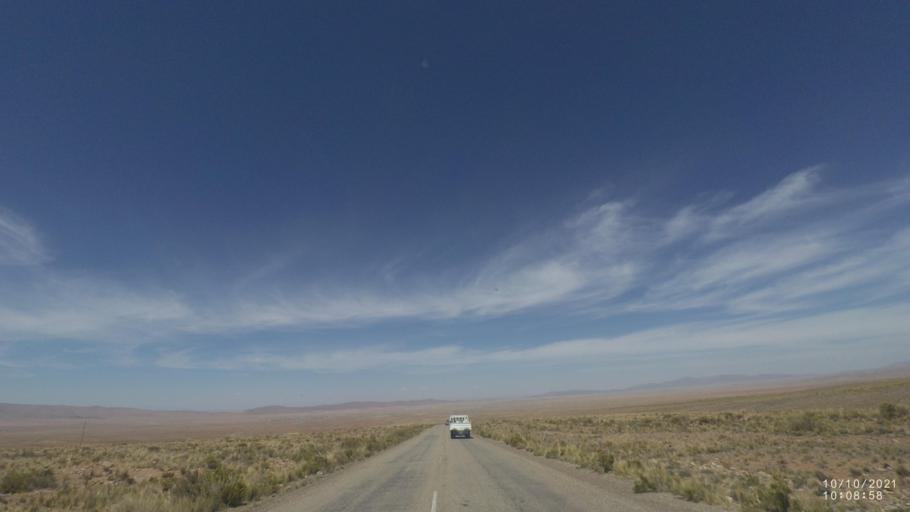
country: BO
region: La Paz
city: Eucaliptus
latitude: -17.3965
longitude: -67.4826
